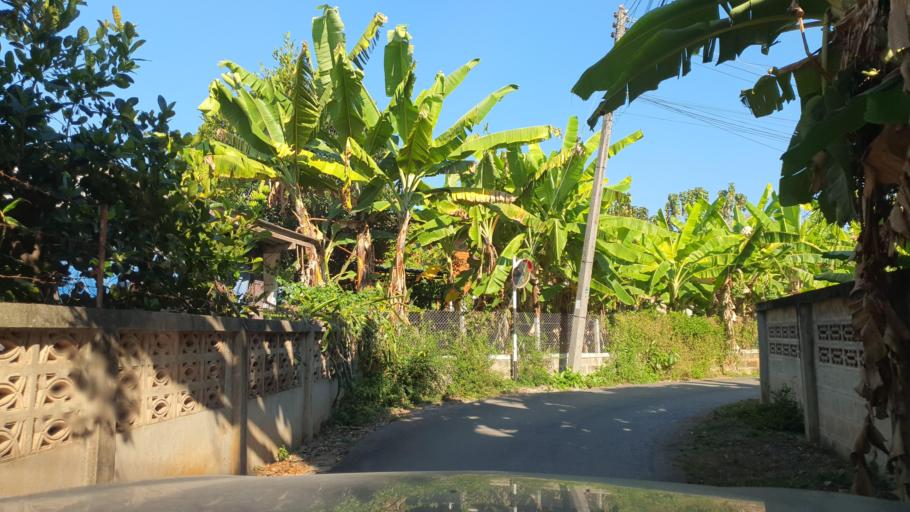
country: TH
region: Chiang Mai
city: Hang Dong
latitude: 18.6956
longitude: 98.9283
